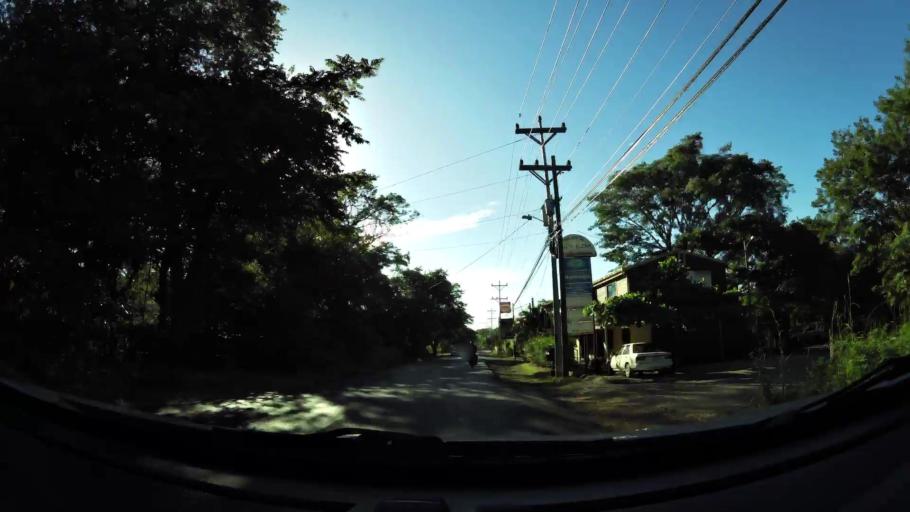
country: CR
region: Guanacaste
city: Sardinal
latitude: 10.5351
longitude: -85.6633
